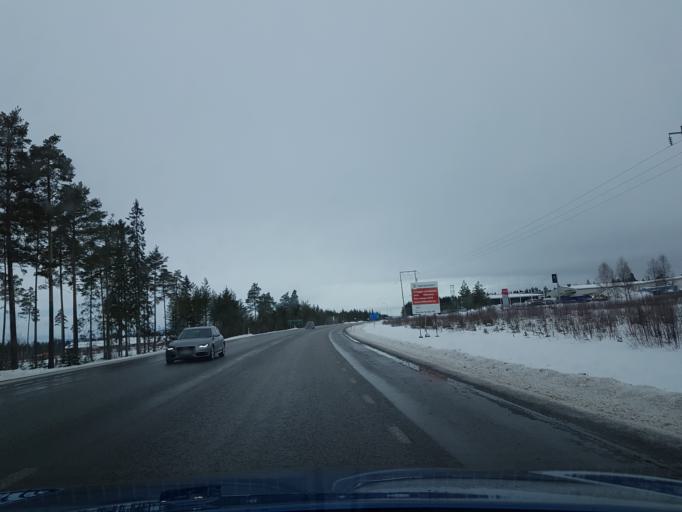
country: SE
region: Dalarna
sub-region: Mora Kommun
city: Mora
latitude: 61.0180
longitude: 14.5884
